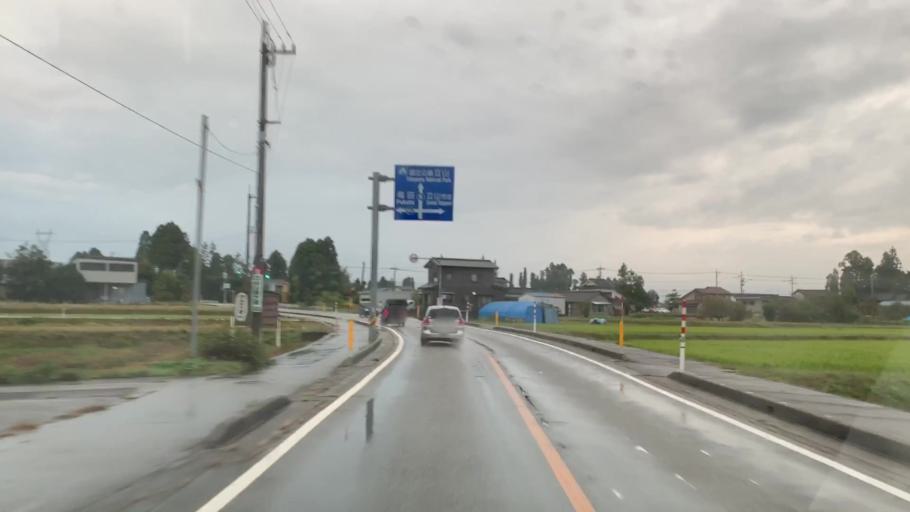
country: JP
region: Toyama
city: Kamiichi
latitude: 36.6633
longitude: 137.3275
